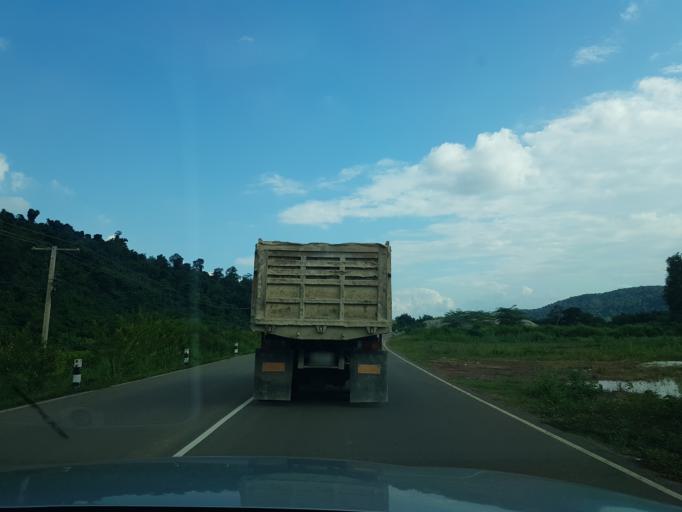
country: TH
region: Nong Khai
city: Sangkhom
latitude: 18.0123
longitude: 102.4005
